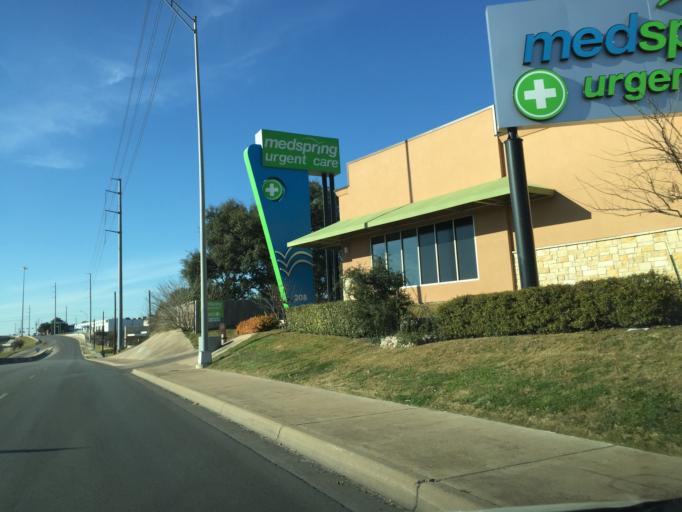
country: US
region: Texas
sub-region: Travis County
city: Austin
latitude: 30.2242
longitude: -97.7647
